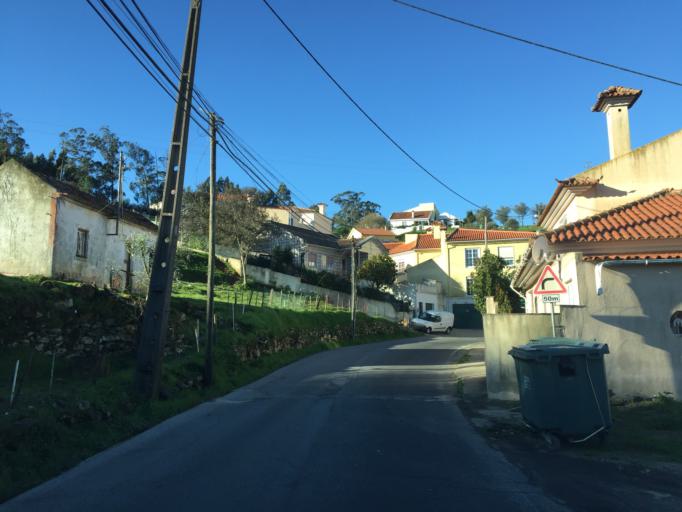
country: PT
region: Lisbon
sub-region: Odivelas
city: Canecas
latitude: 38.8235
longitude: -9.2379
